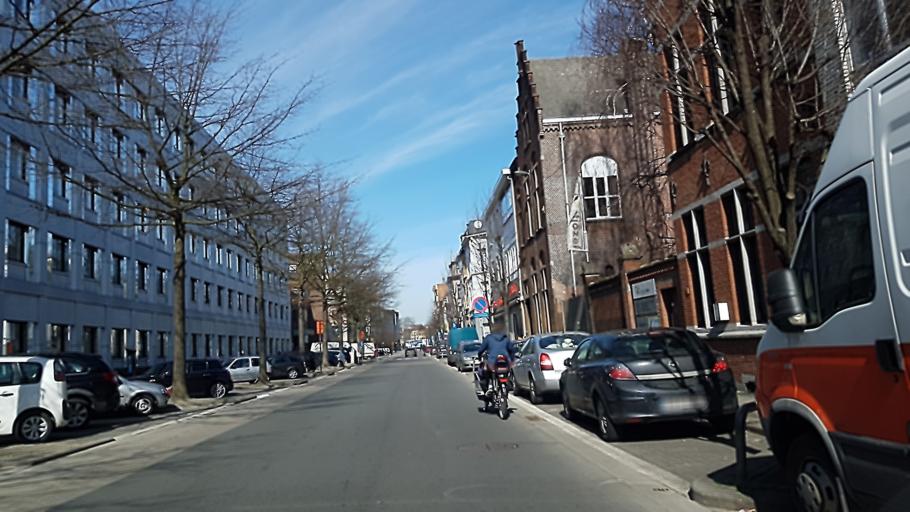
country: BE
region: Flanders
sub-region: Provincie Antwerpen
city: Antwerpen
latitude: 51.2237
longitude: 4.4367
